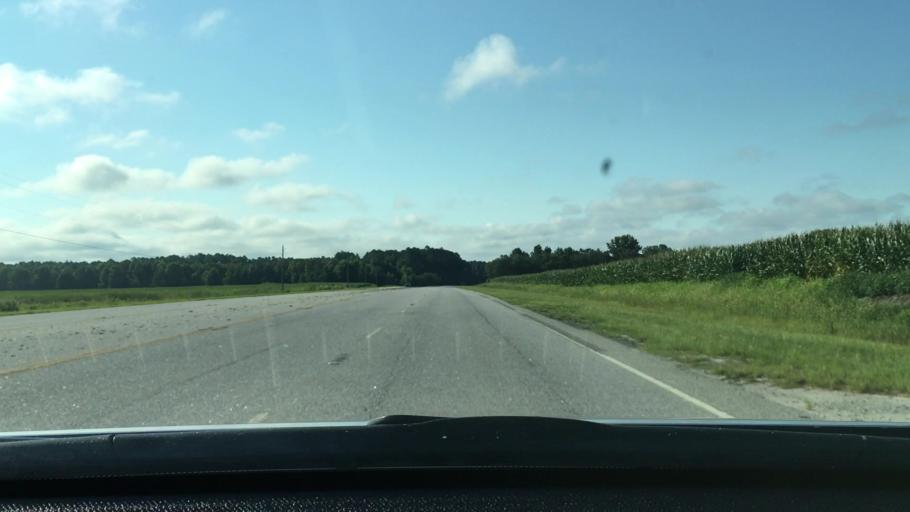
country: US
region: South Carolina
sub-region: Clarendon County
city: Manning
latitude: 33.7788
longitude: -80.2439
